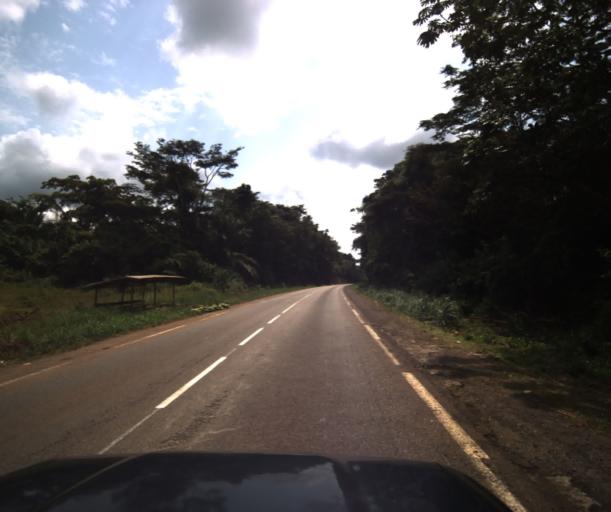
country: CM
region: Centre
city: Eseka
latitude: 3.8734
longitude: 10.6268
